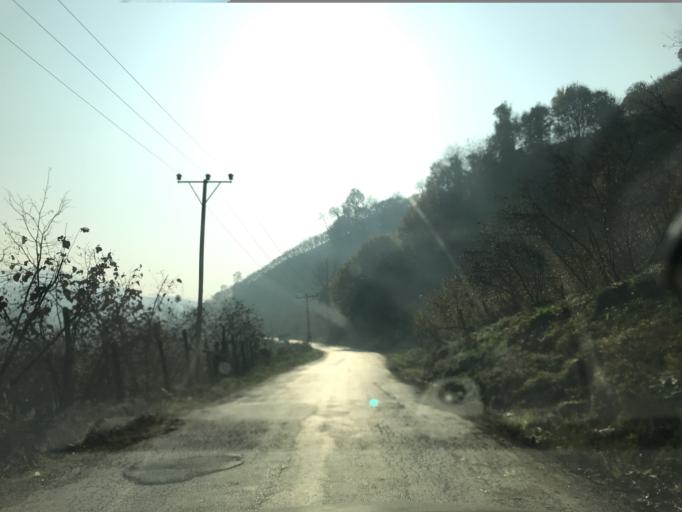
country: TR
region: Duzce
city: Cumayeri
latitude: 40.9097
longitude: 30.9459
